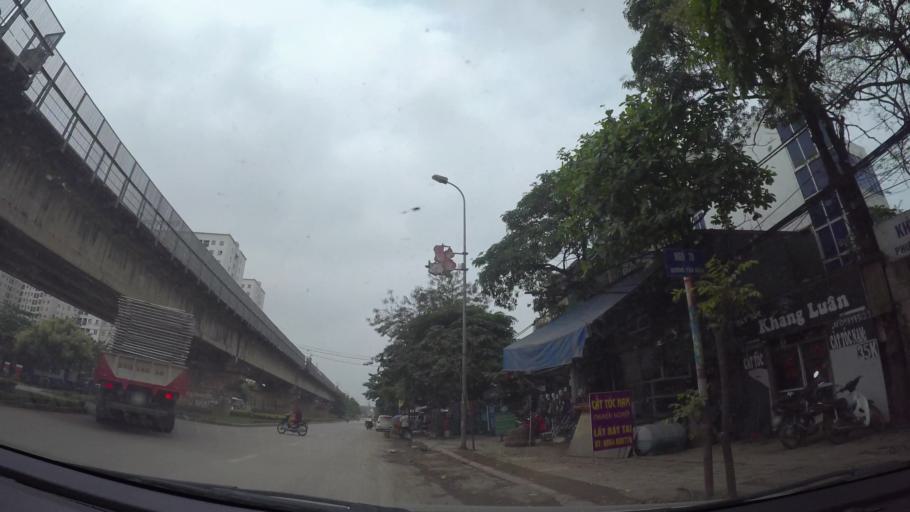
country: VN
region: Ha Noi
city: Tay Ho
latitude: 21.0818
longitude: 105.7857
